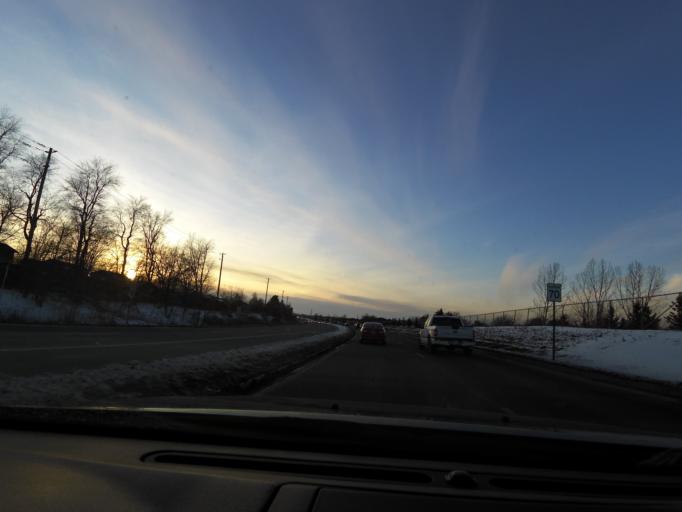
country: CA
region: Ontario
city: Hamilton
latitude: 43.1964
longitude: -79.7965
